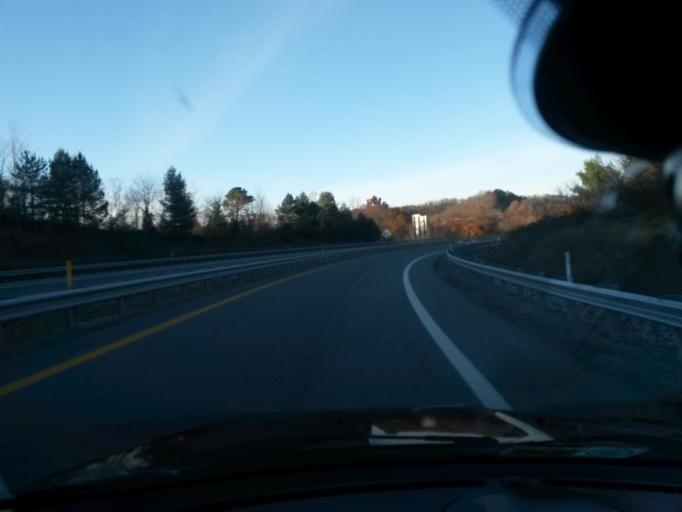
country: US
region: West Virginia
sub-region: Raleigh County
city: Prosperity
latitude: 37.8327
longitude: -81.2167
